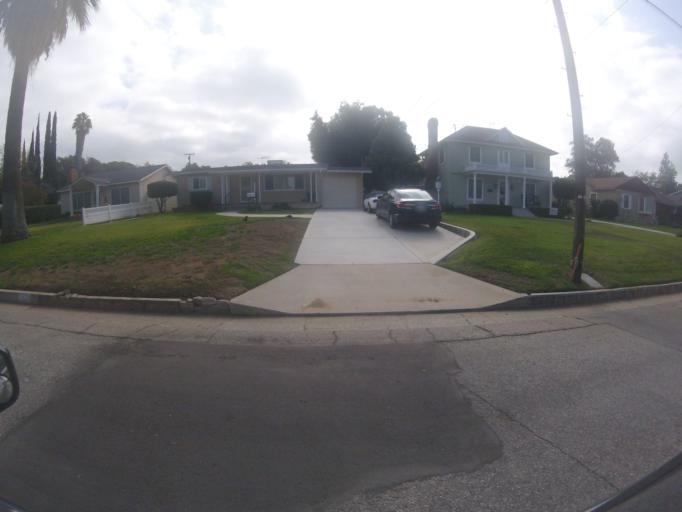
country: US
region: California
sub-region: San Bernardino County
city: Redlands
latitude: 34.0382
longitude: -117.1853
